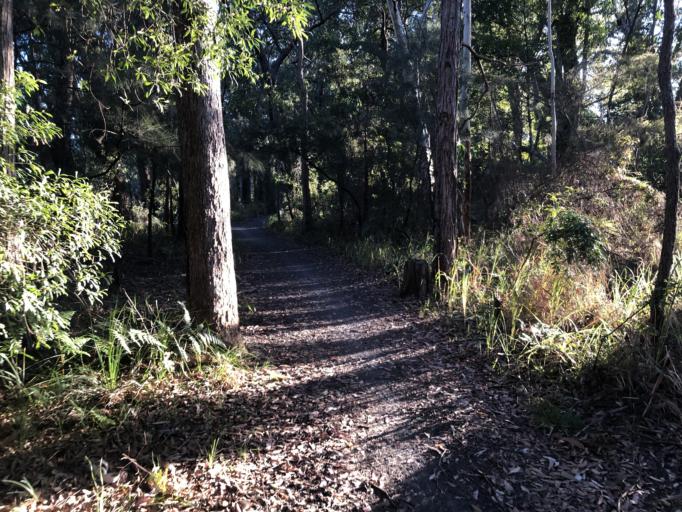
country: AU
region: New South Wales
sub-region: Coffs Harbour
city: Coffs Harbour
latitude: -30.2902
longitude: 153.1266
